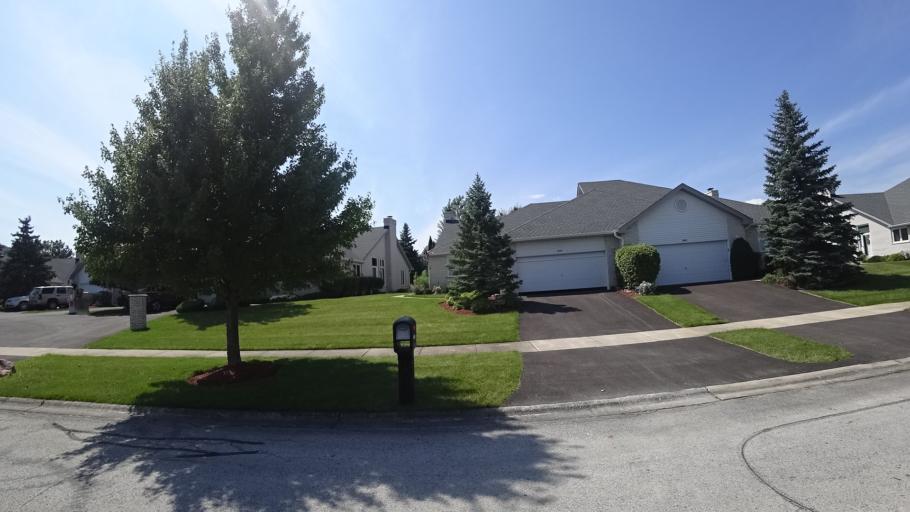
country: US
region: Illinois
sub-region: Cook County
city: Orland Hills
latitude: 41.5590
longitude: -87.8360
